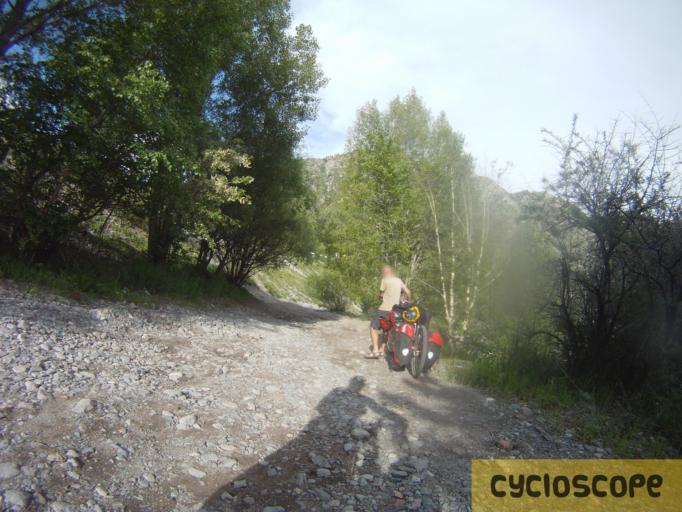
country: KZ
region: Almaty Oblysy
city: Esik
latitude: 43.2558
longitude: 77.4835
